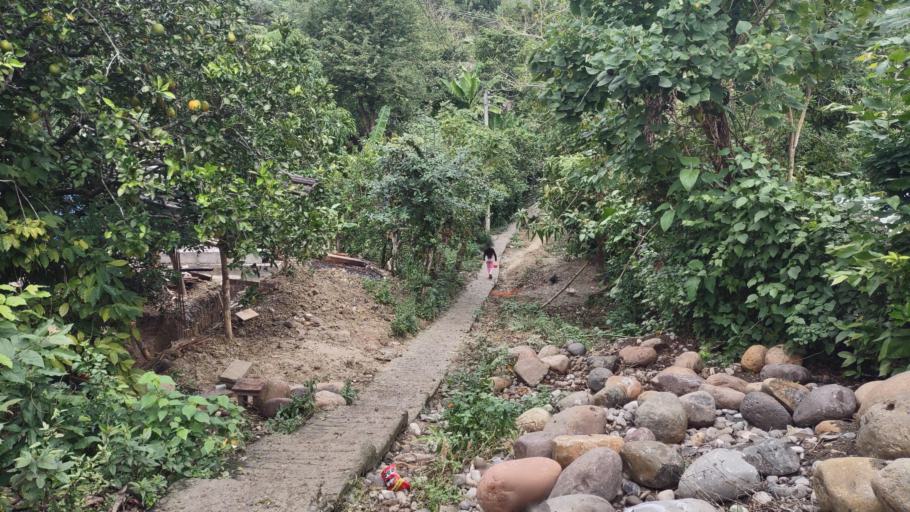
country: MX
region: Puebla
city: Espinal
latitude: 20.2636
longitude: -97.3724
